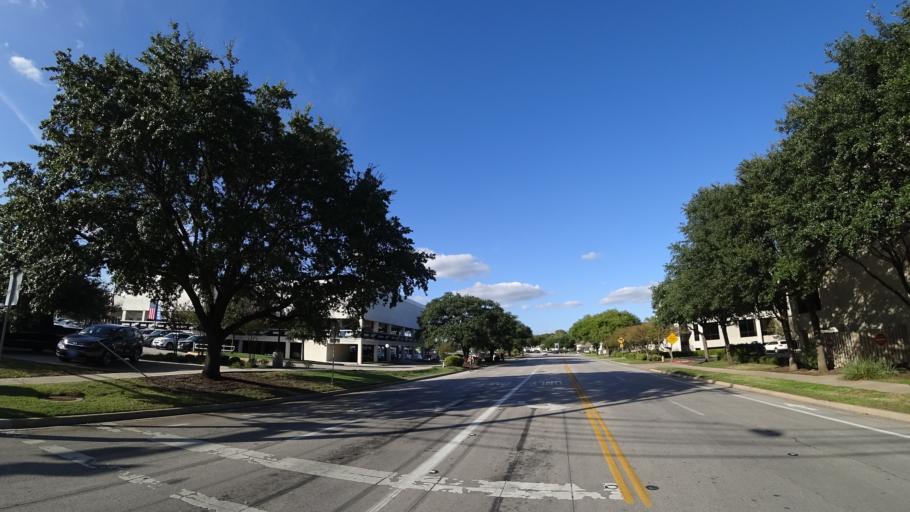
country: US
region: Texas
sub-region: Williamson County
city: Jollyville
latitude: 30.3665
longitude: -97.7385
